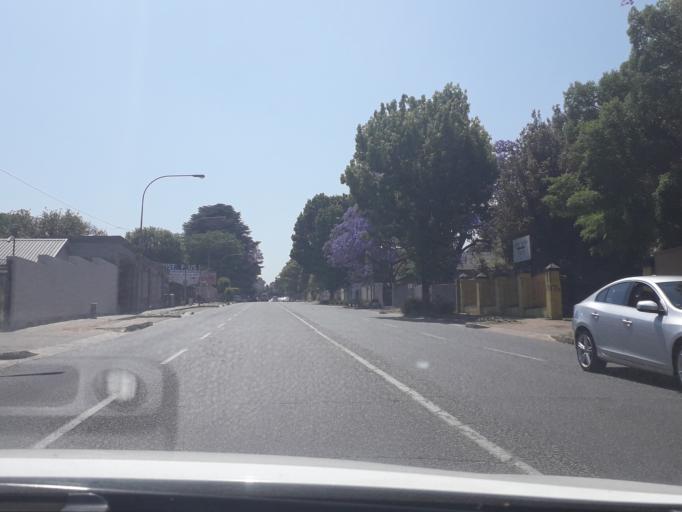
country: ZA
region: Gauteng
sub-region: City of Johannesburg Metropolitan Municipality
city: Johannesburg
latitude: -26.1273
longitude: 28.0781
